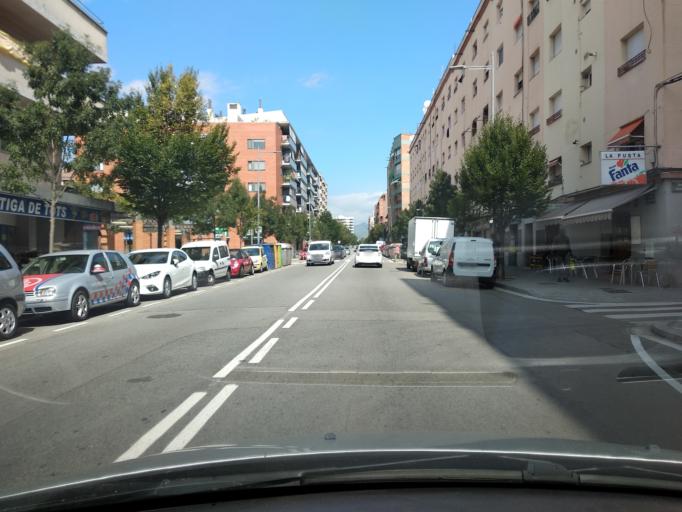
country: ES
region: Catalonia
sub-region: Provincia de Barcelona
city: Granollers
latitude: 41.6052
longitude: 2.2831
